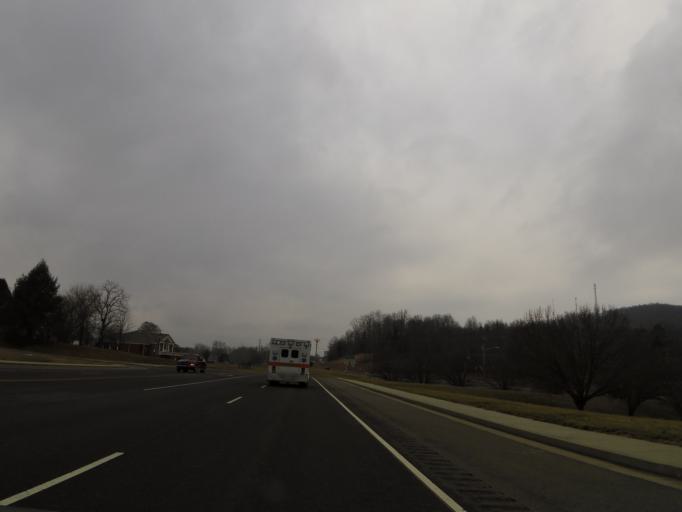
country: US
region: Tennessee
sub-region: Morgan County
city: Wartburg
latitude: 36.1025
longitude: -84.5860
